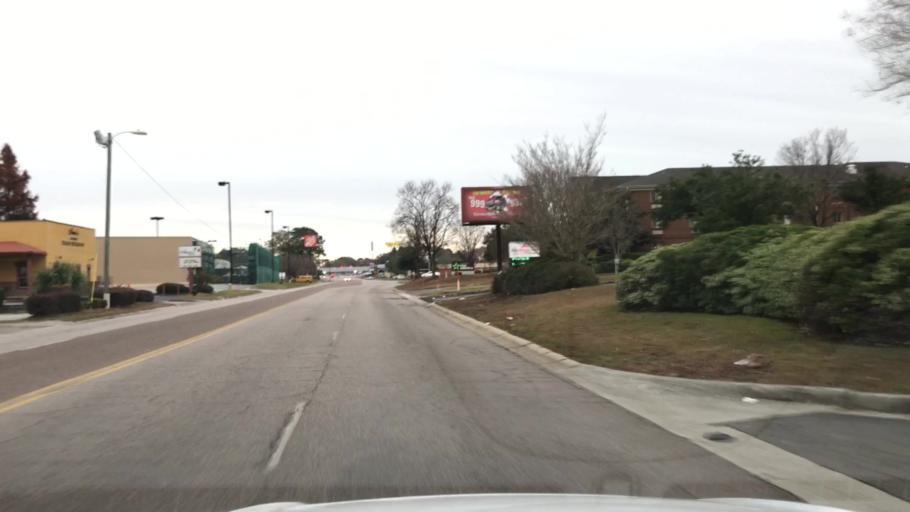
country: US
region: South Carolina
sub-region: Berkeley County
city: Hanahan
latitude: 32.9401
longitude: -80.0466
